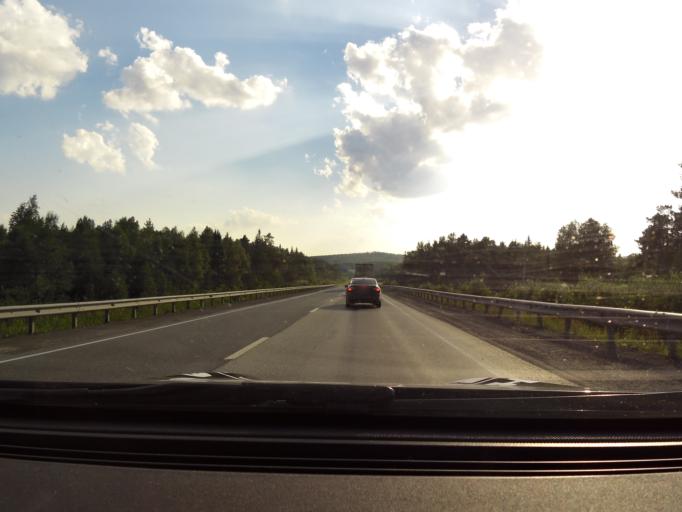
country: RU
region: Sverdlovsk
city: Talitsa
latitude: 56.8479
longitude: 60.0383
